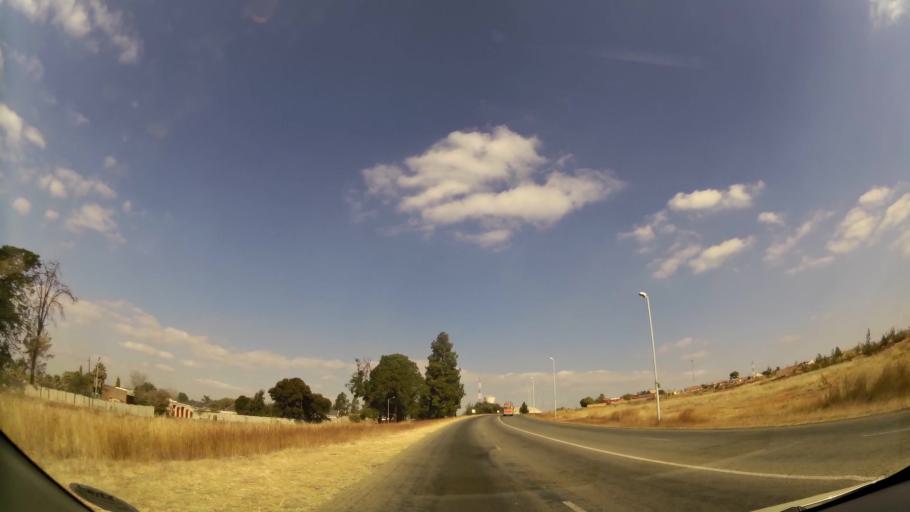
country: ZA
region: Gauteng
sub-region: West Rand District Municipality
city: Krugersdorp
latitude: -26.0671
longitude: 27.7616
